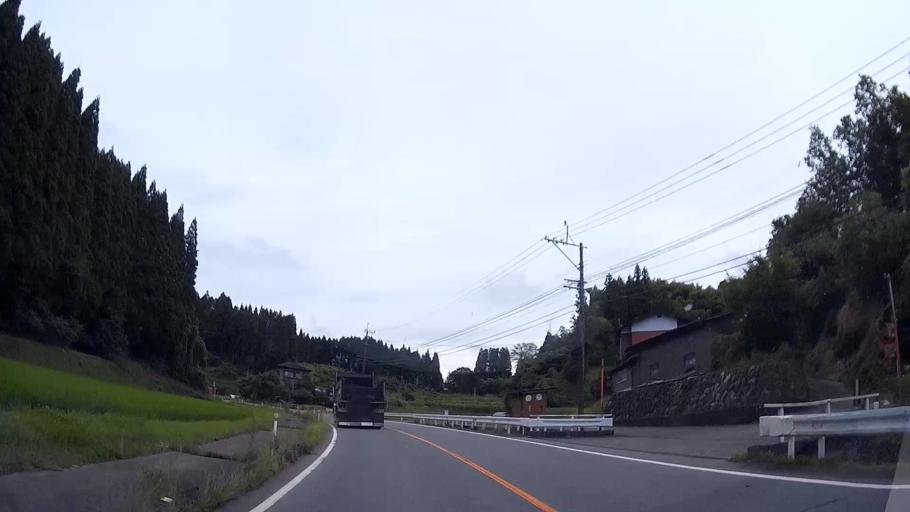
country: JP
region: Kumamoto
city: Aso
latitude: 33.1242
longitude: 131.0410
